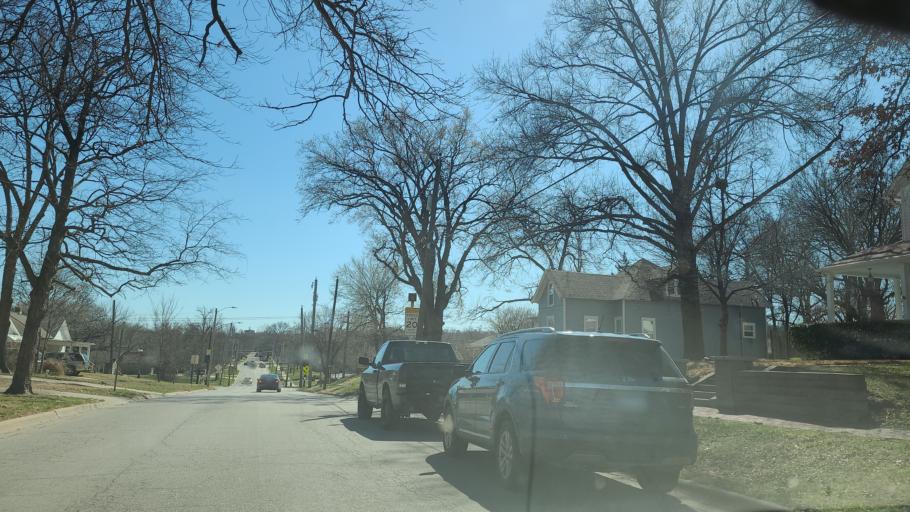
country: US
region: Kansas
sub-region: Douglas County
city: Lawrence
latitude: 38.9759
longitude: -95.2476
